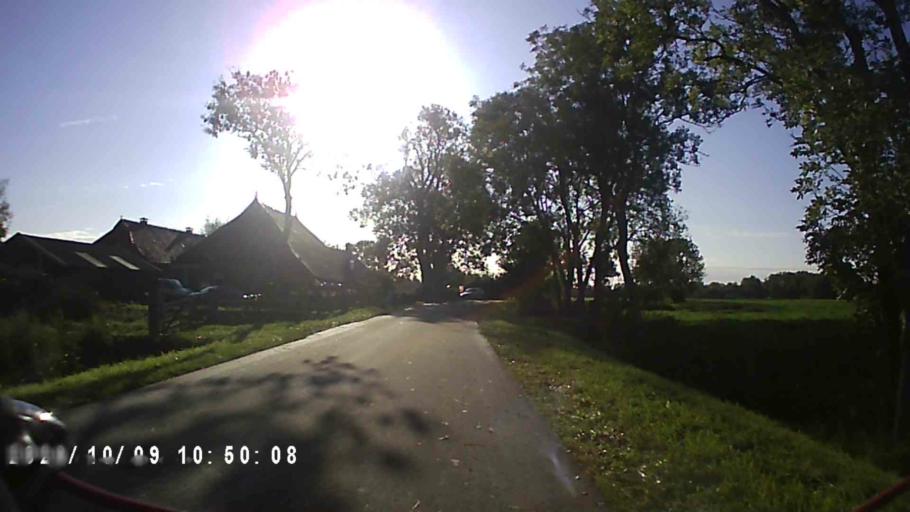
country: NL
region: Groningen
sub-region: Gemeente Groningen
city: Korrewegwijk
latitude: 53.2508
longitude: 6.5491
